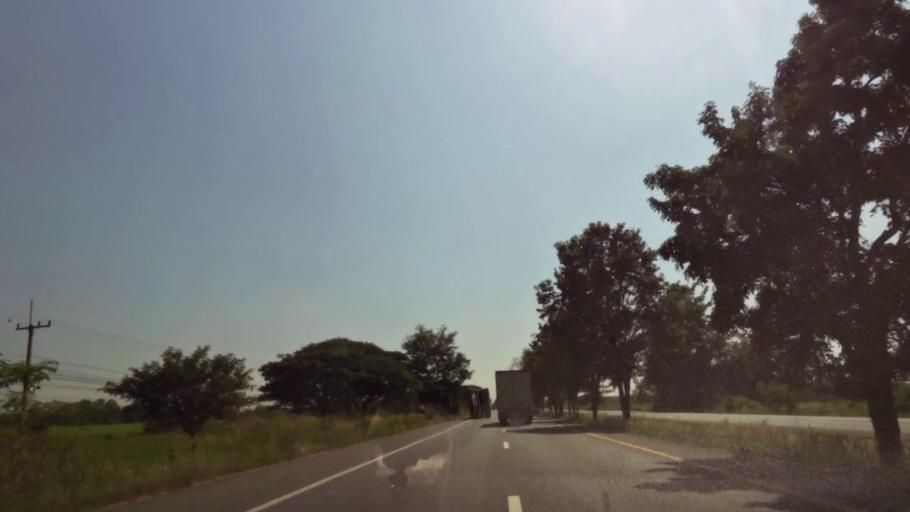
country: TH
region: Nakhon Sawan
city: Kao Liao
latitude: 15.9052
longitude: 100.1127
